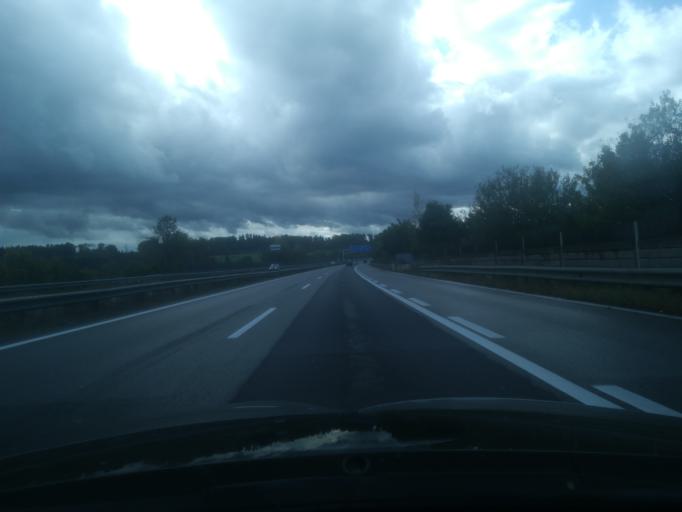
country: AT
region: Upper Austria
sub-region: Politischer Bezirk Urfahr-Umgebung
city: Engerwitzdorf
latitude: 48.3461
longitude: 14.4527
